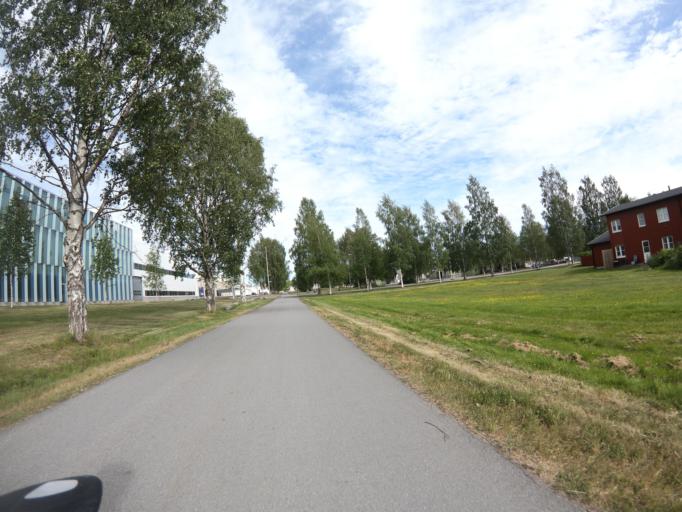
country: SE
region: Vaesterbotten
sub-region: Umea Kommun
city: Umea
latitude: 63.8184
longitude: 20.2560
